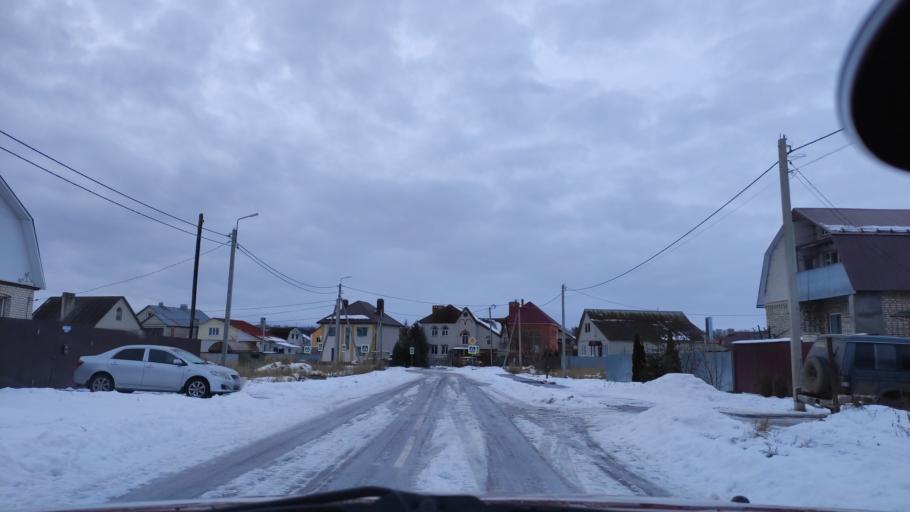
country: RU
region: Tambov
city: Komsomolets
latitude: 52.7626
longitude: 41.3643
